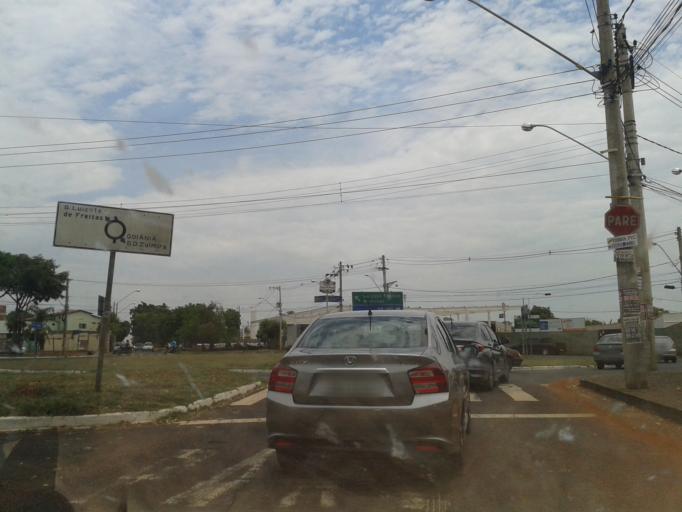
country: BR
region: Minas Gerais
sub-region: Uberlandia
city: Uberlandia
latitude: -18.9111
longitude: -48.3173
